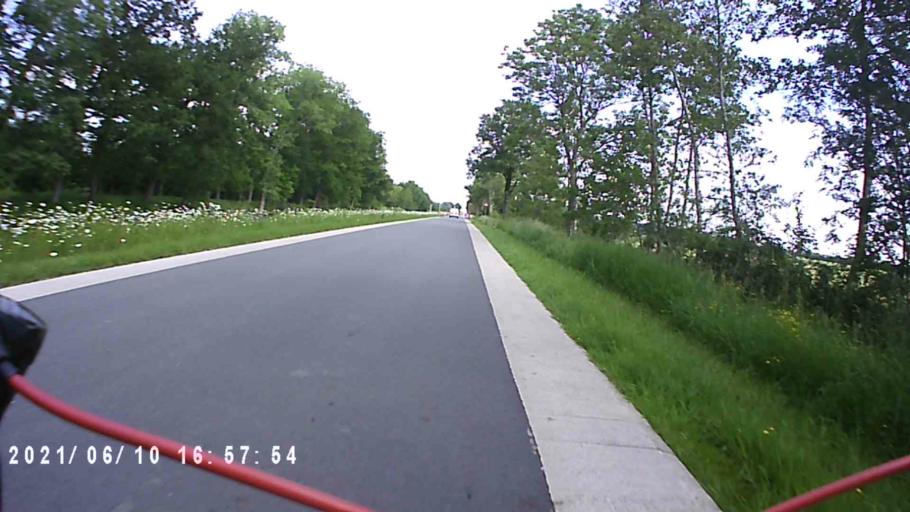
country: NL
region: Friesland
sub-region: Gemeente Kollumerland en Nieuwkruisland
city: Kollum
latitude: 53.2715
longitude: 6.1453
